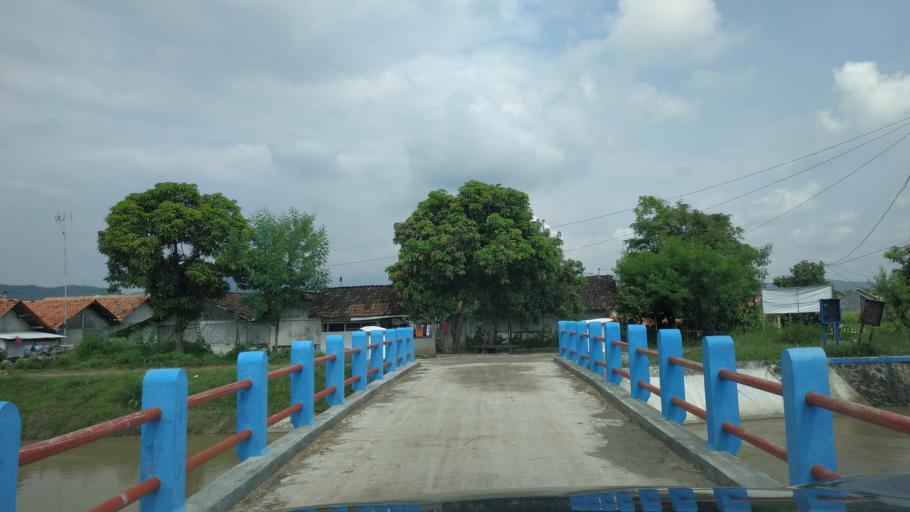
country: ID
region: Central Java
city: Margasari
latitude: -7.0923
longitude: 108.9836
